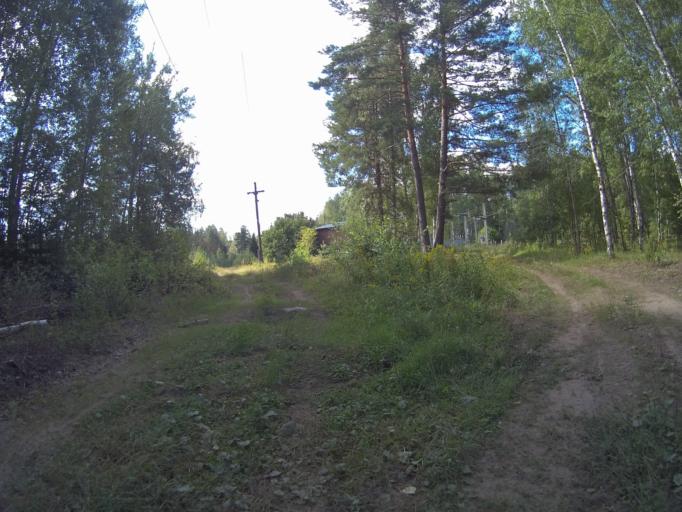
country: RU
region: Vladimir
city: Raduzhnyy
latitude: 55.8994
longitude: 40.1978
